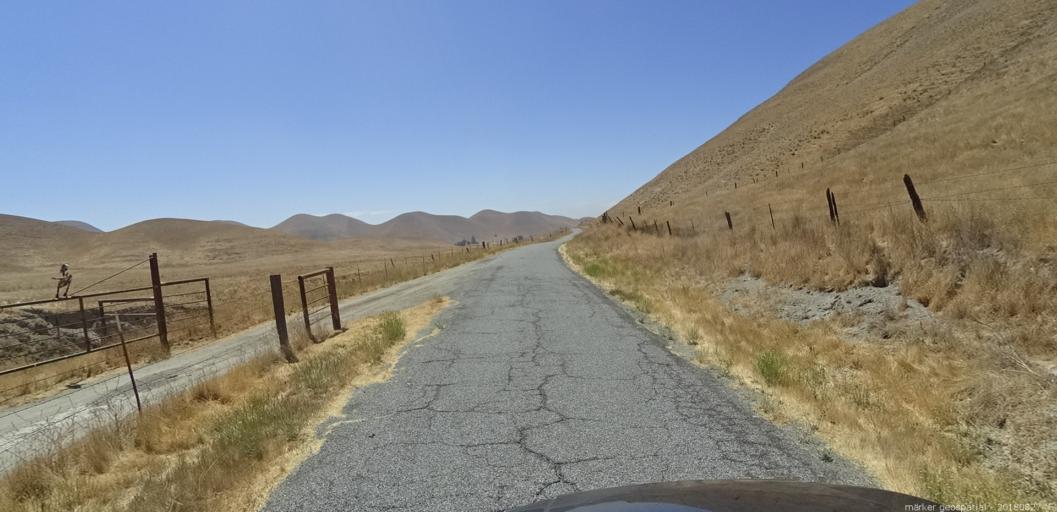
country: US
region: California
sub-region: Monterey County
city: King City
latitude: 36.1105
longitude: -120.8759
